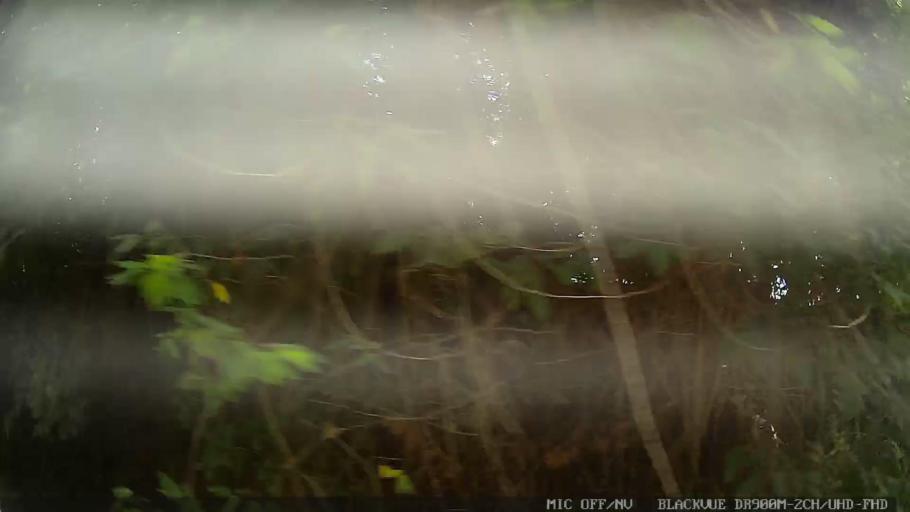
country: BR
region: Sao Paulo
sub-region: Braganca Paulista
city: Braganca Paulista
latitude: -23.0282
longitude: -46.4739
